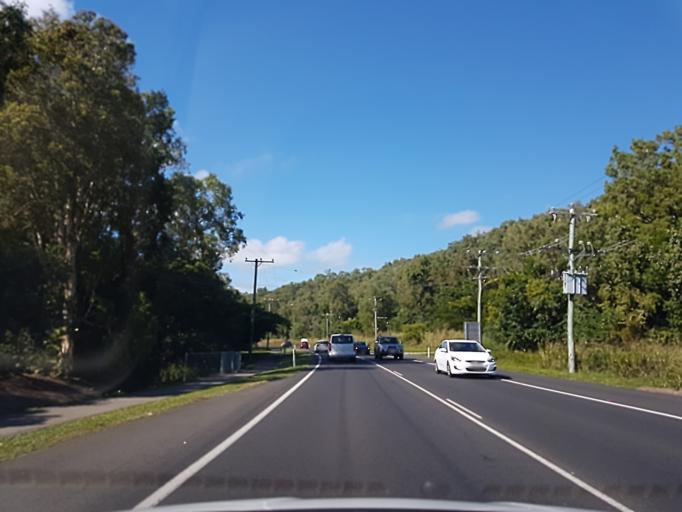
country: AU
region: Queensland
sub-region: Cairns
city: Palm Cove
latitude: -16.7682
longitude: 145.6697
